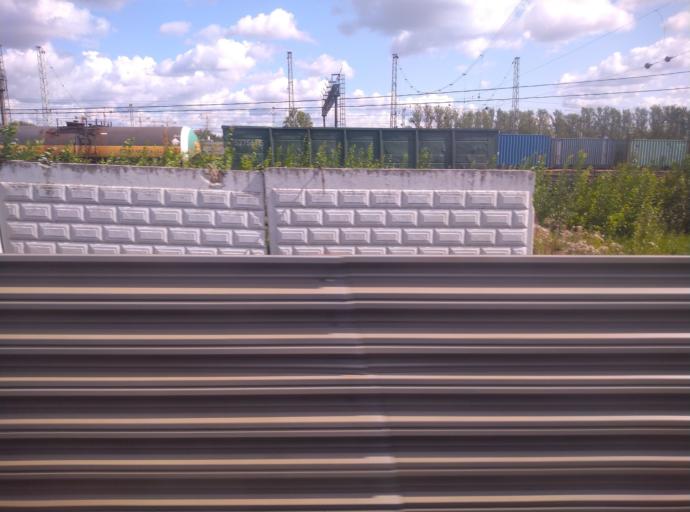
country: RU
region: St.-Petersburg
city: Kupchino
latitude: 59.8832
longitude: 30.4027
